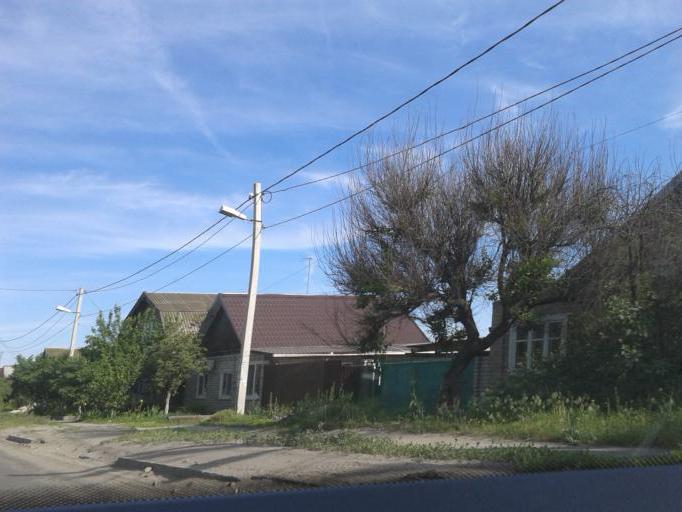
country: RU
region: Volgograd
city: Volgograd
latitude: 48.6950
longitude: 44.4472
